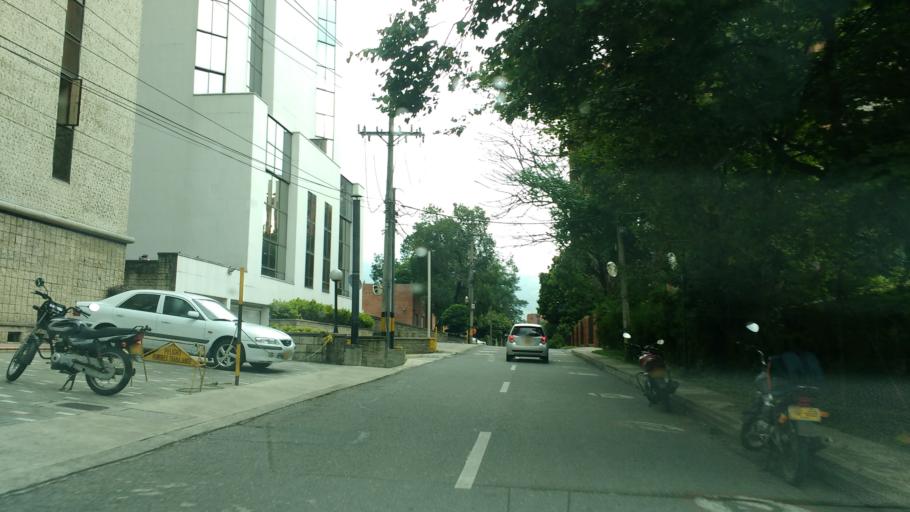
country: CO
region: Antioquia
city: Envigado
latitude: 6.1904
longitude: -75.5776
